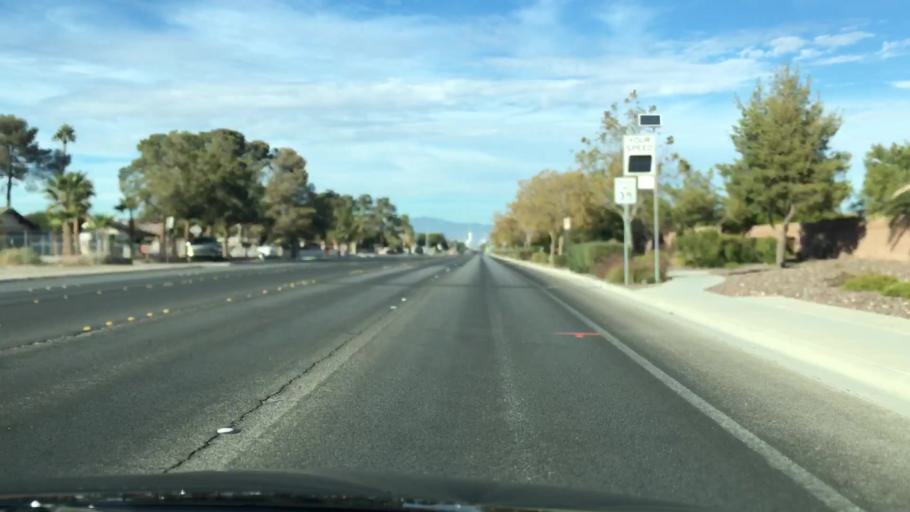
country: US
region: Nevada
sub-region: Clark County
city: Paradise
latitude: 36.0465
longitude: -115.1543
